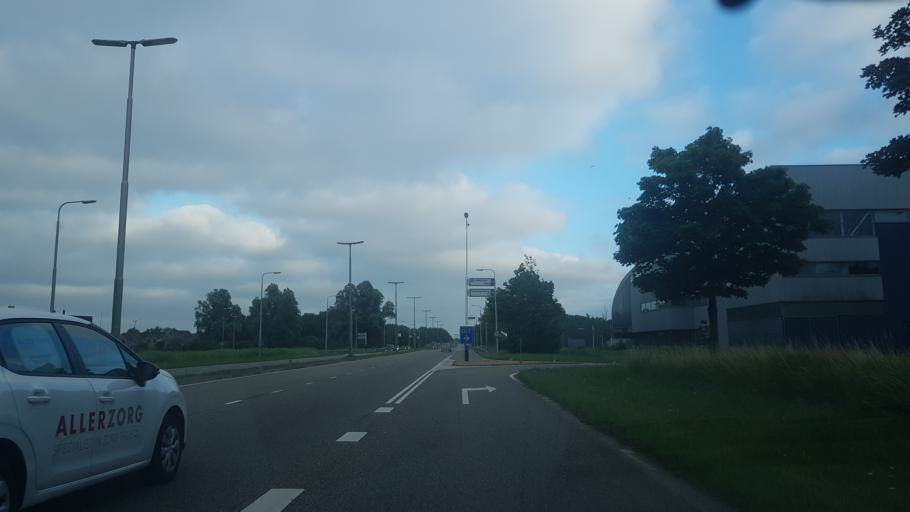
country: NL
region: Friesland
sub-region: Gemeente Leeuwarden
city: Camminghaburen
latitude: 53.2127
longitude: 5.8299
